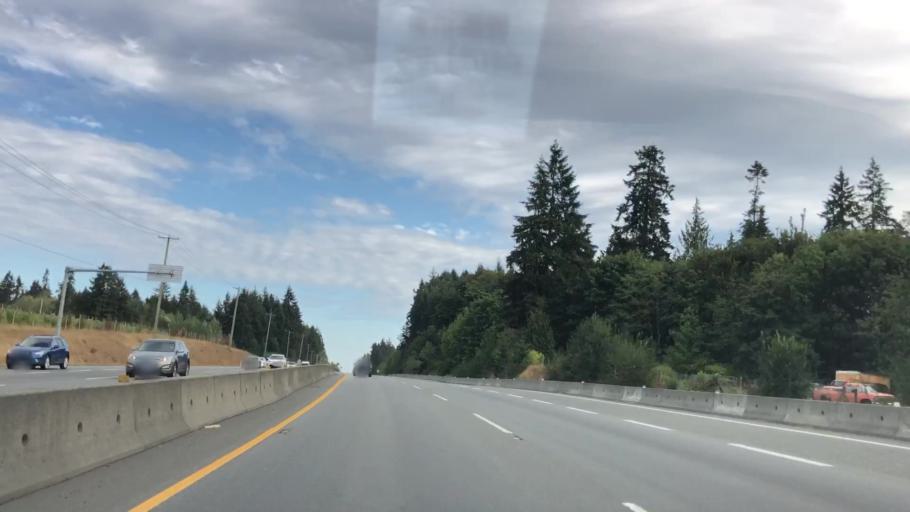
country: CA
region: British Columbia
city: Duncan
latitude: 48.7069
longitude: -123.6068
